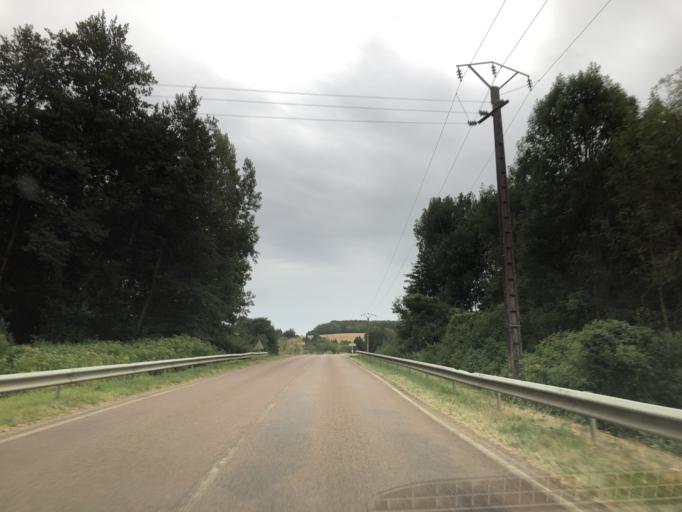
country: FR
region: Bourgogne
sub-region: Departement de l'Yonne
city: Saint-Julien-du-Sault
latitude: 47.9342
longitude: 3.2416
